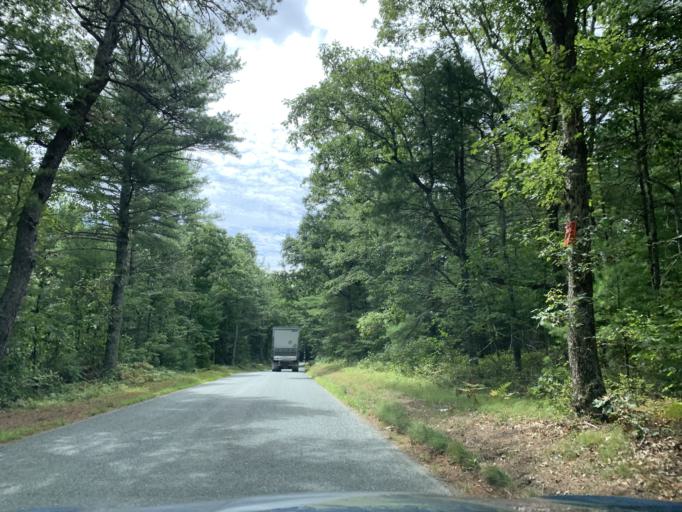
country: US
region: Rhode Island
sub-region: Kent County
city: West Greenwich
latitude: 41.5807
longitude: -71.6188
